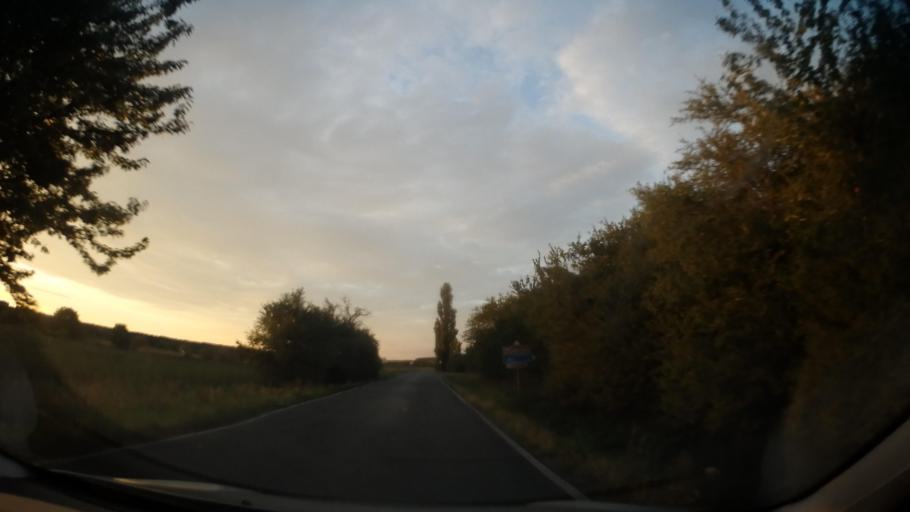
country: CZ
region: Central Bohemia
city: Loucen
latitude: 50.2549
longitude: 15.0247
